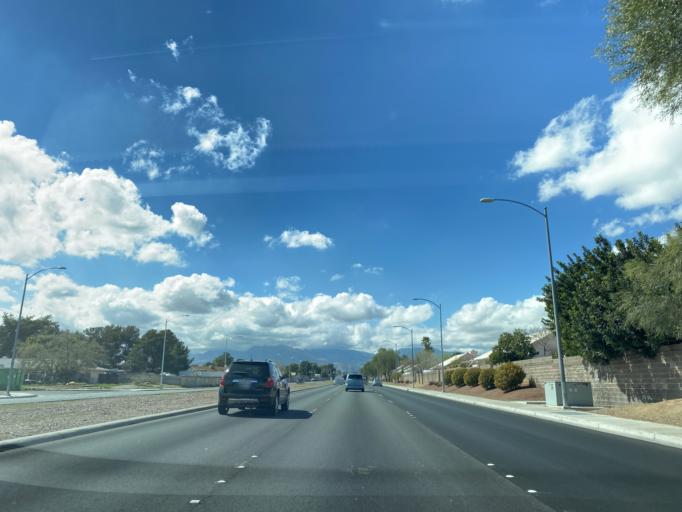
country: US
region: Nevada
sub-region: Clark County
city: Las Vegas
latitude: 36.2389
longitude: -115.2128
